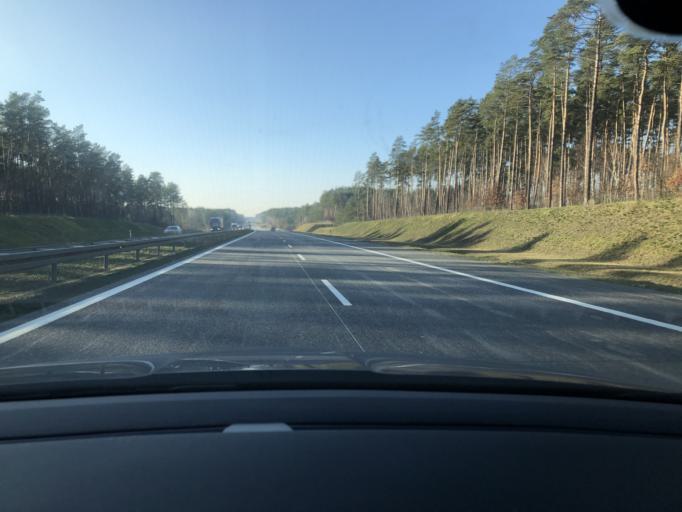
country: PL
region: Lubusz
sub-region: Powiat sulecinski
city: Torzym
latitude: 52.3269
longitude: 15.1451
